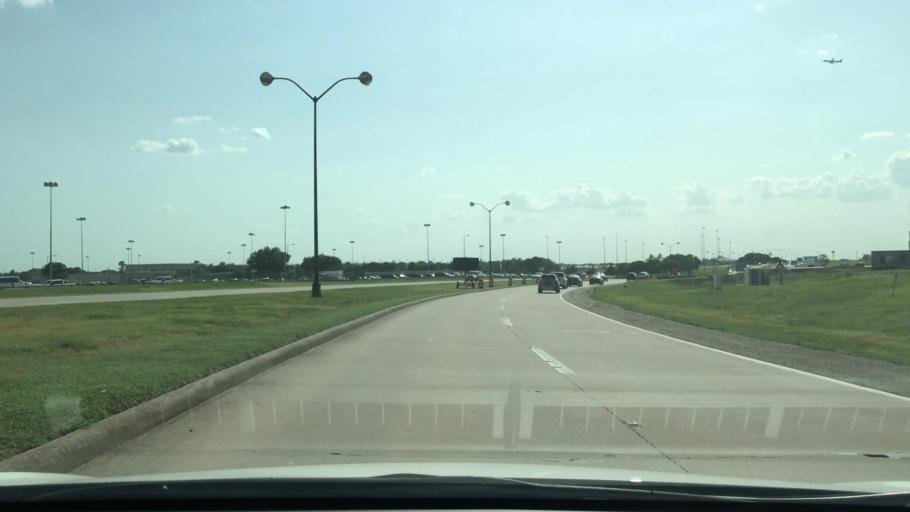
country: US
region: Texas
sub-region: Tarrant County
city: Euless
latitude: 32.8625
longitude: -97.0260
